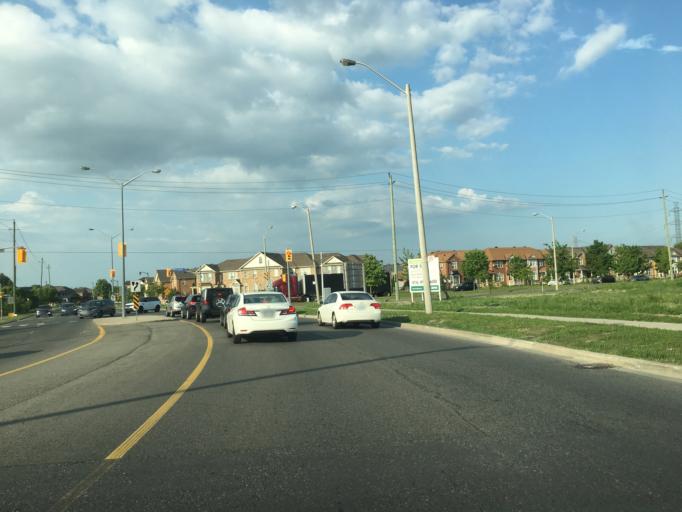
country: CA
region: Ontario
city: Markham
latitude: 43.8267
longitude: -79.2353
